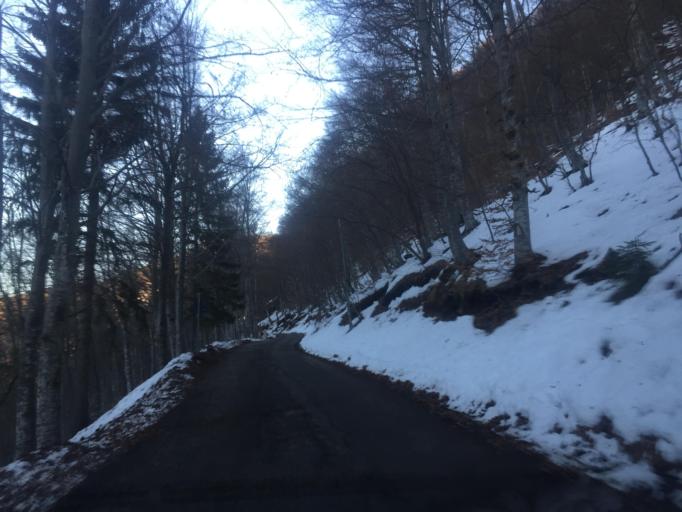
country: IT
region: Friuli Venezia Giulia
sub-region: Provincia di Udine
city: Lauco
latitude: 46.4496
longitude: 12.9309
